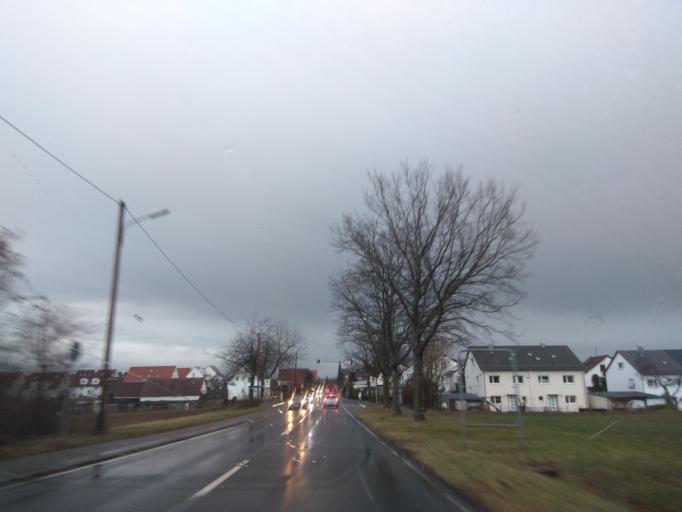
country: DE
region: Baden-Wuerttemberg
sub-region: Regierungsbezirk Stuttgart
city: Steinenbronn
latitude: 48.6980
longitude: 9.1181
